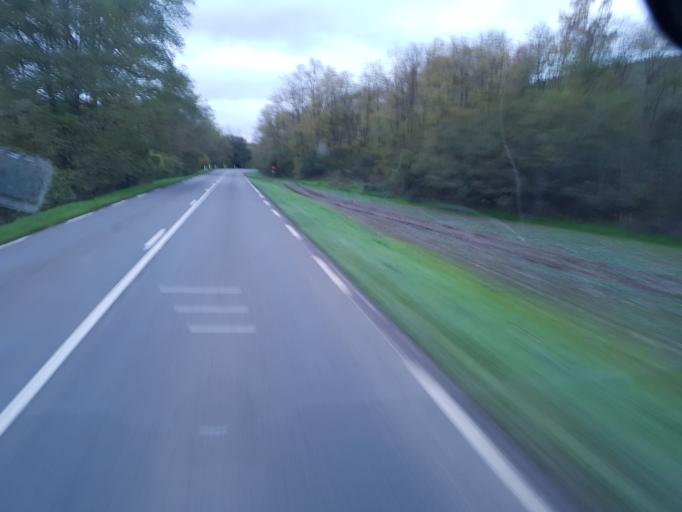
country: FR
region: Picardie
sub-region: Departement de l'Aisne
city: Coincy
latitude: 49.1413
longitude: 3.3875
